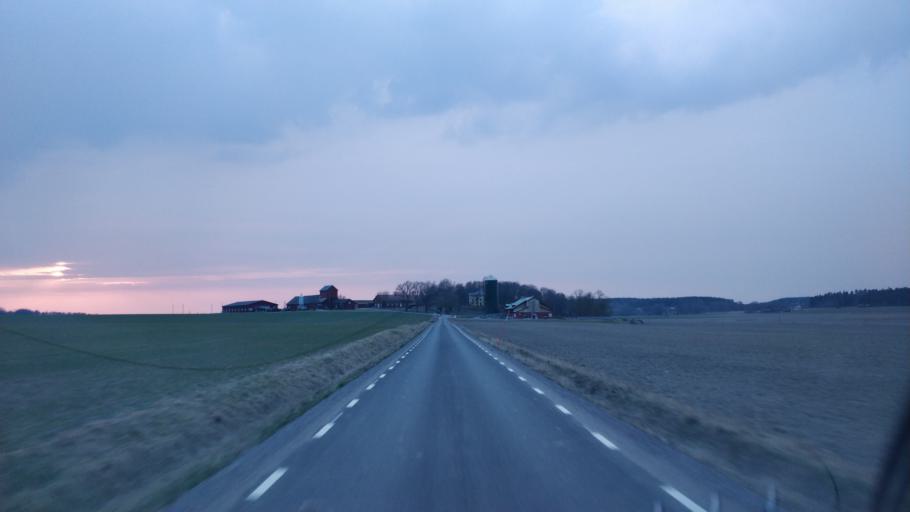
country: SE
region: Uppsala
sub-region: Enkopings Kommun
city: Orsundsbro
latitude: 59.7373
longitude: 17.1883
